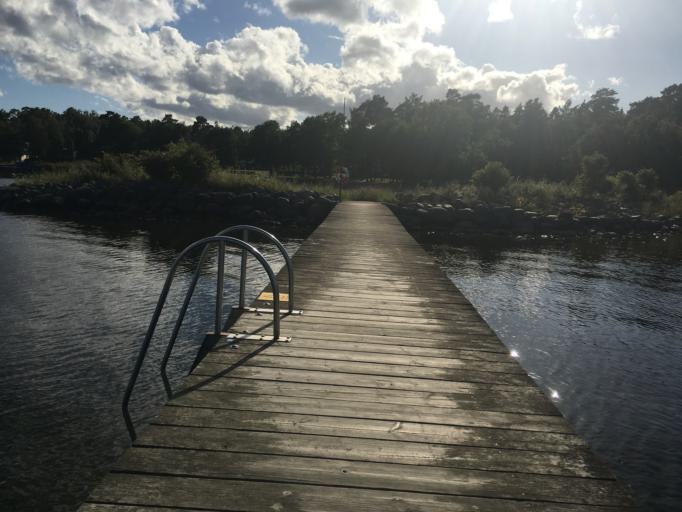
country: SE
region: Kalmar
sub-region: Kalmar Kommun
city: Kalmar
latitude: 56.7047
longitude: 16.3747
